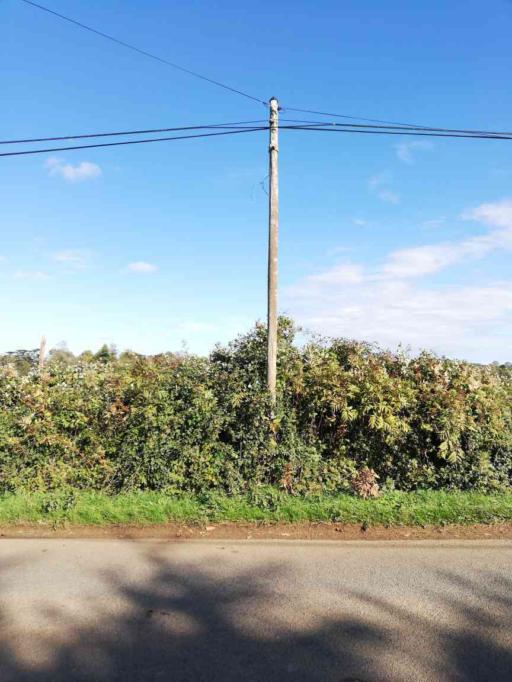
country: FR
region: Pays de la Loire
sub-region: Departement de la Vendee
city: Le Champ-Saint-Pere
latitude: 46.4965
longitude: -1.3431
